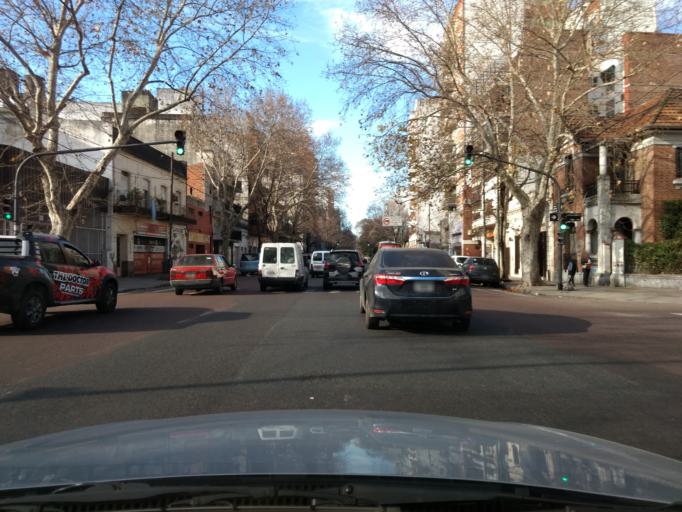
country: AR
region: Buenos Aires F.D.
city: Villa Santa Rita
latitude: -34.6302
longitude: -58.4863
